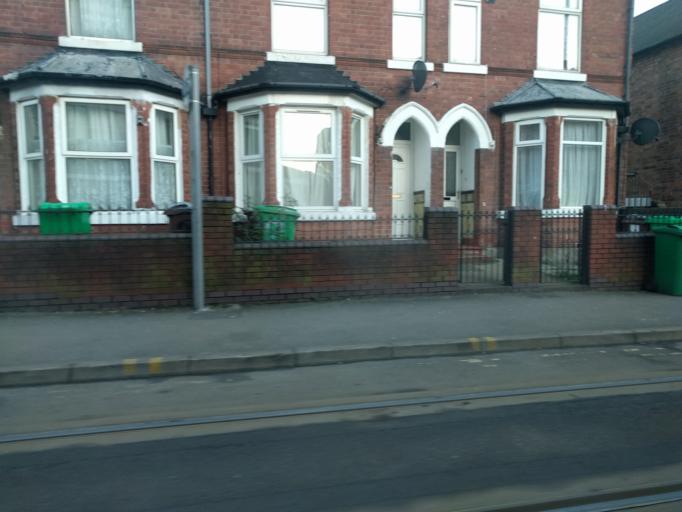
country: GB
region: England
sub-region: Nottingham
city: Nottingham
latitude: 52.9663
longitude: -1.1679
